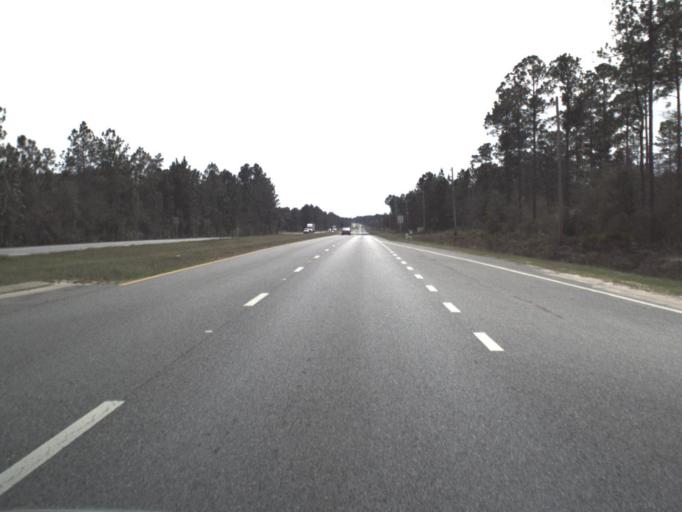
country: US
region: Florida
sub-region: Bay County
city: Youngstown
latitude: 30.5088
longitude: -85.4118
